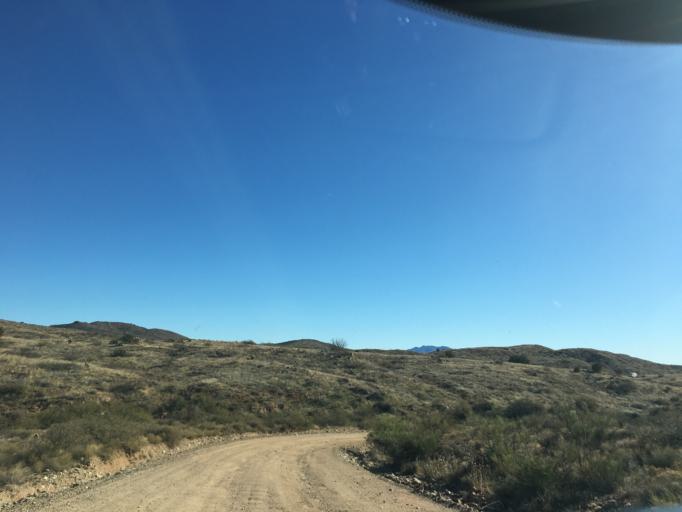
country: US
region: Arizona
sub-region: Yavapai County
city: Cordes Lakes
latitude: 34.2703
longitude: -112.1082
